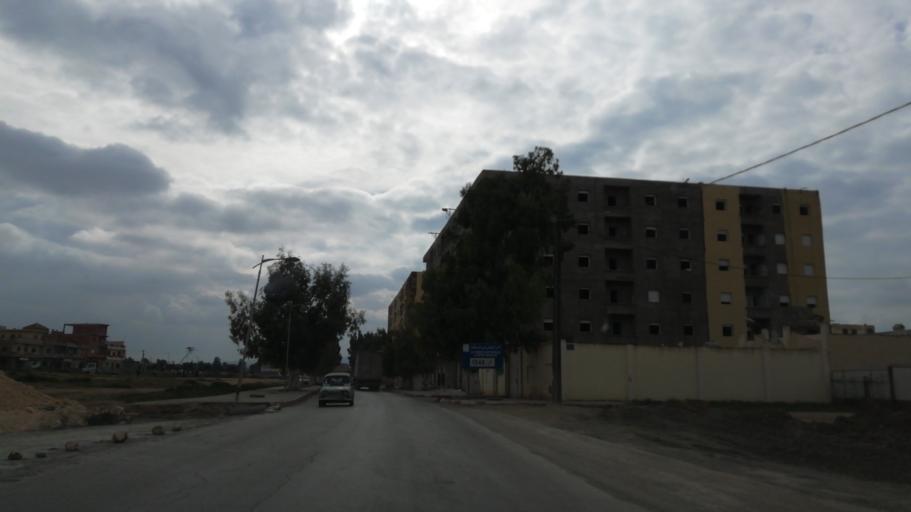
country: DZ
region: Oran
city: Sidi ech Chahmi
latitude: 35.5577
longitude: -0.4481
